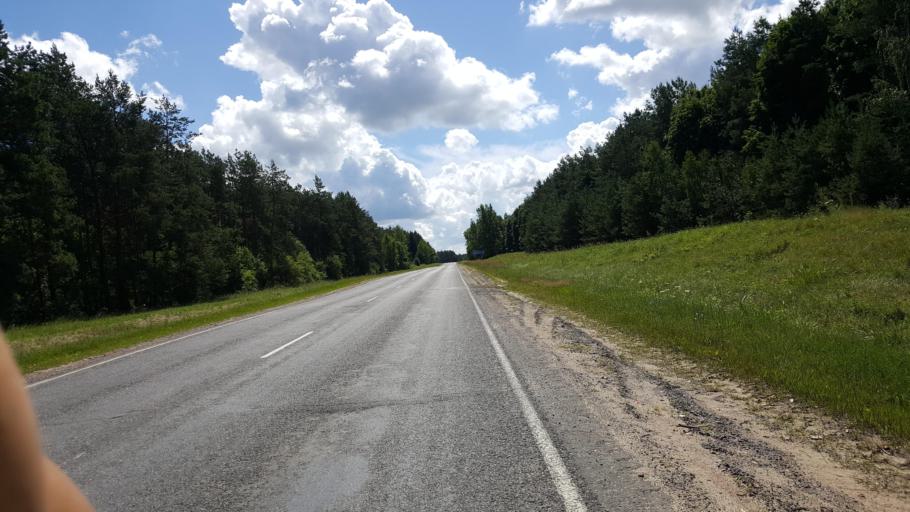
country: BY
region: Brest
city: Kamyanyets
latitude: 52.3902
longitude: 23.8404
